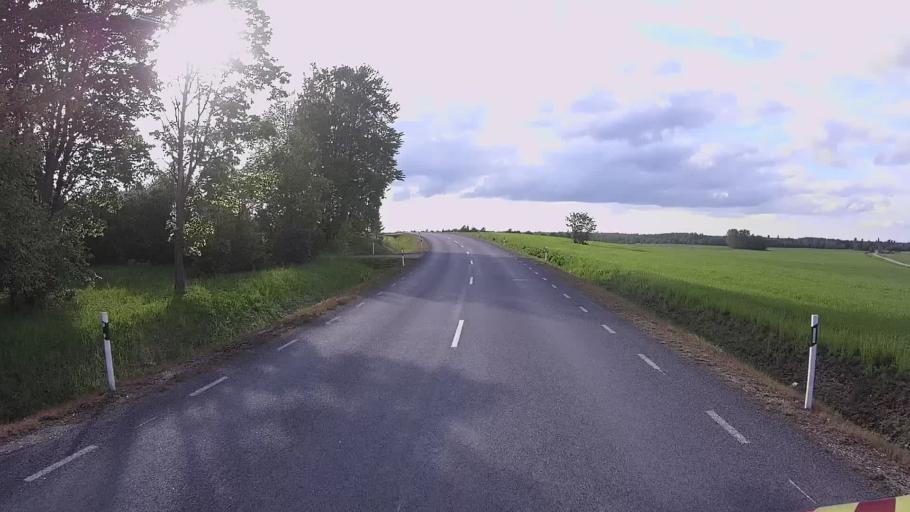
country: EE
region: Jogevamaa
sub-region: Mustvee linn
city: Mustvee
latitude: 59.0437
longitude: 27.0559
